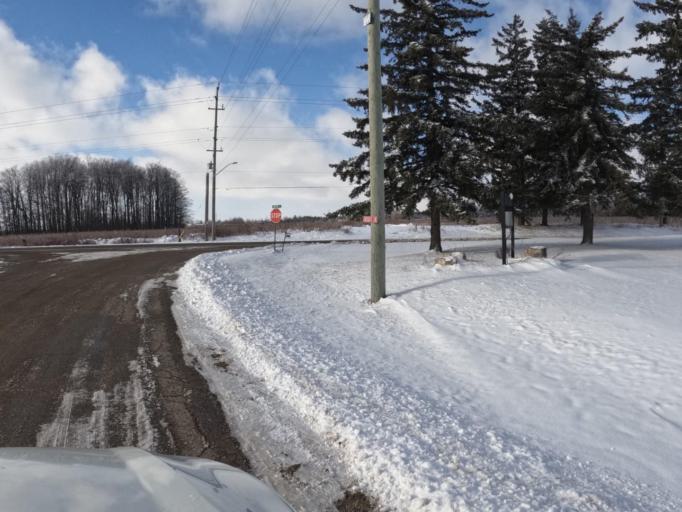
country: CA
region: Ontario
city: Orangeville
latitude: 43.8877
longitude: -80.3122
